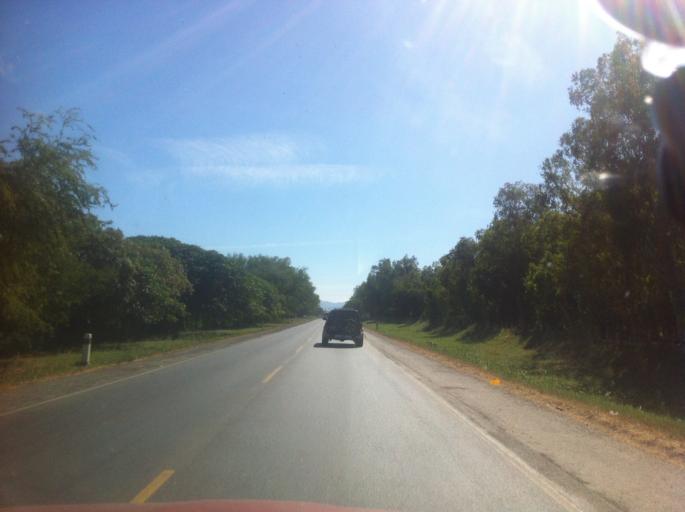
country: NI
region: Managua
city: Tipitapa
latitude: 12.2131
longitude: -86.0991
